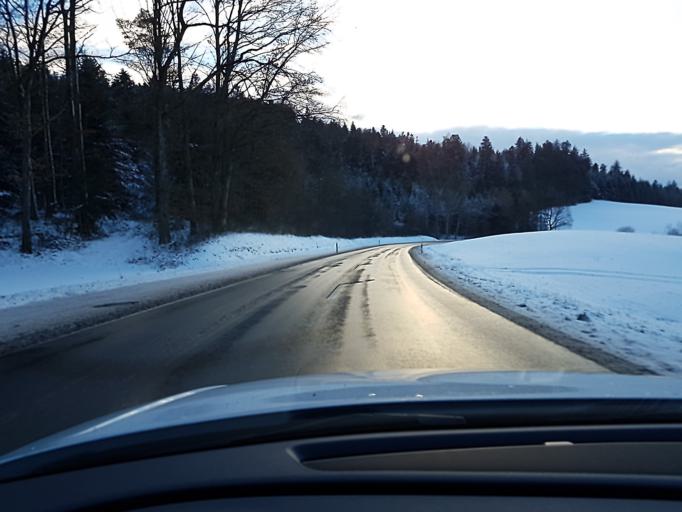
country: DE
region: Baden-Wuerttemberg
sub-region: Regierungsbezirk Stuttgart
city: Fichtenberg
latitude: 48.9816
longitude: 9.6816
